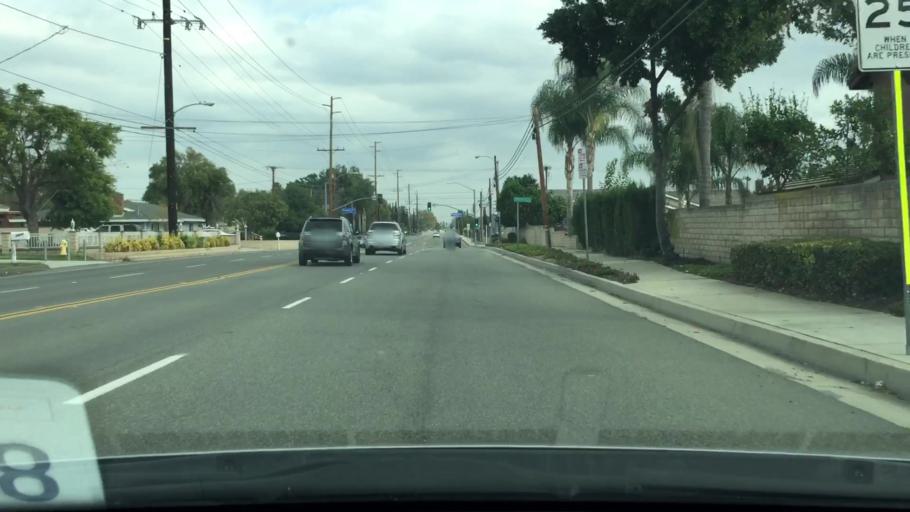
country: US
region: California
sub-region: San Bernardino County
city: Chino
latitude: 34.0115
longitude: -117.7214
